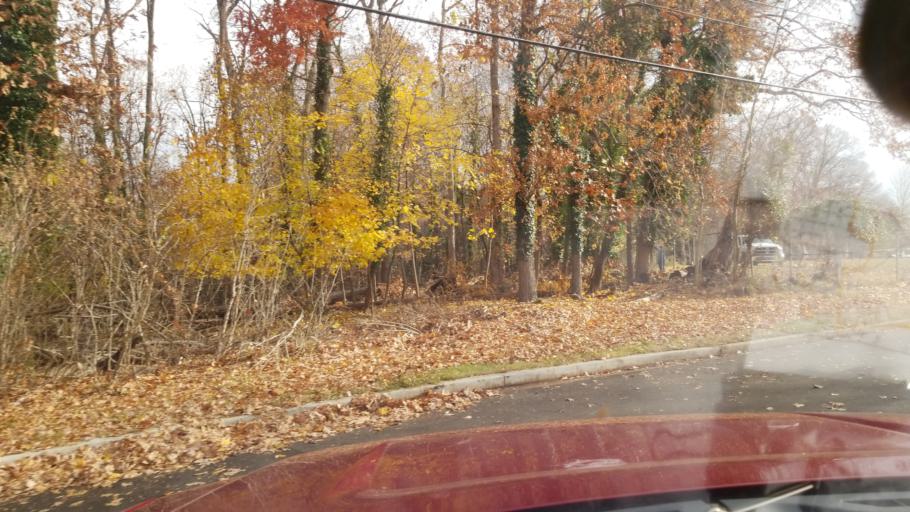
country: US
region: Maryland
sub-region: Prince George's County
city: Silver Hill
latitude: 38.8656
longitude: -76.9574
